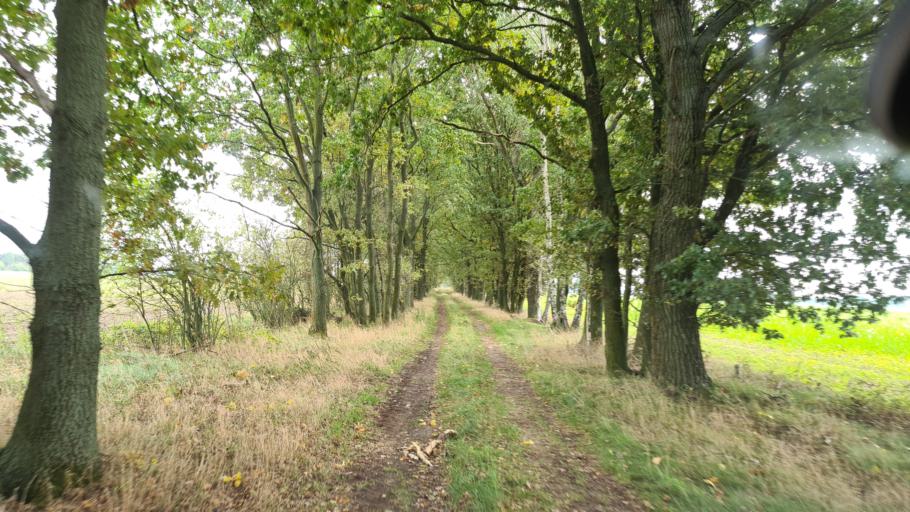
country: DE
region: Brandenburg
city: Schonewalde
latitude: 51.6835
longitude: 13.5608
